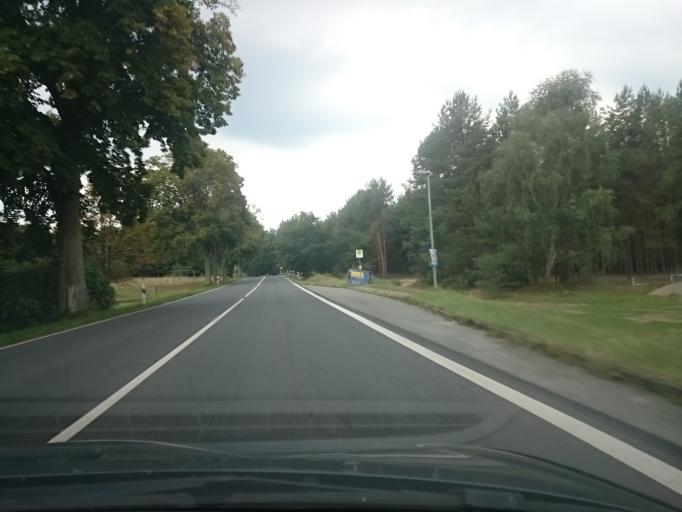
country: DE
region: Brandenburg
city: Furstenberg
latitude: 53.2520
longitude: 13.1138
